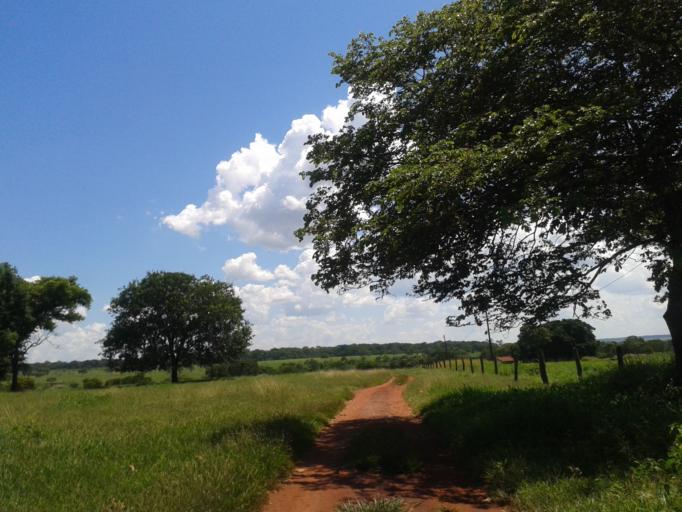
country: BR
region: Minas Gerais
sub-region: Santa Vitoria
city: Santa Vitoria
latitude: -19.1064
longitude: -50.5212
